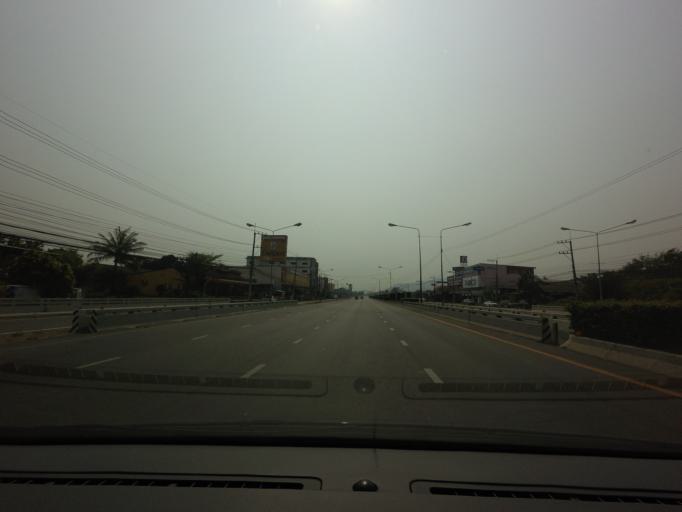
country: TH
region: Prachuap Khiri Khan
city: Pran Buri
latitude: 12.3828
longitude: 99.8954
